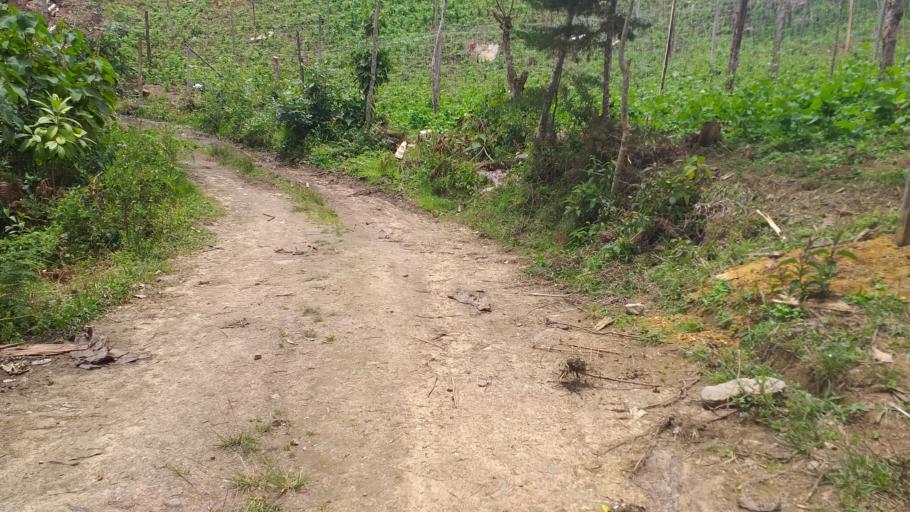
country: CO
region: Cundinamarca
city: Tenza
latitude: 5.0740
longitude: -73.4585
